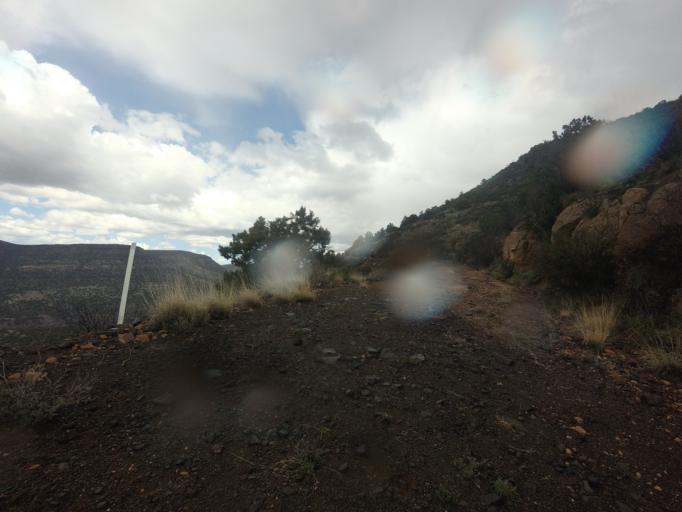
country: US
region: Arizona
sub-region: Gila County
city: Pine
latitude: 34.4063
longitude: -111.5923
